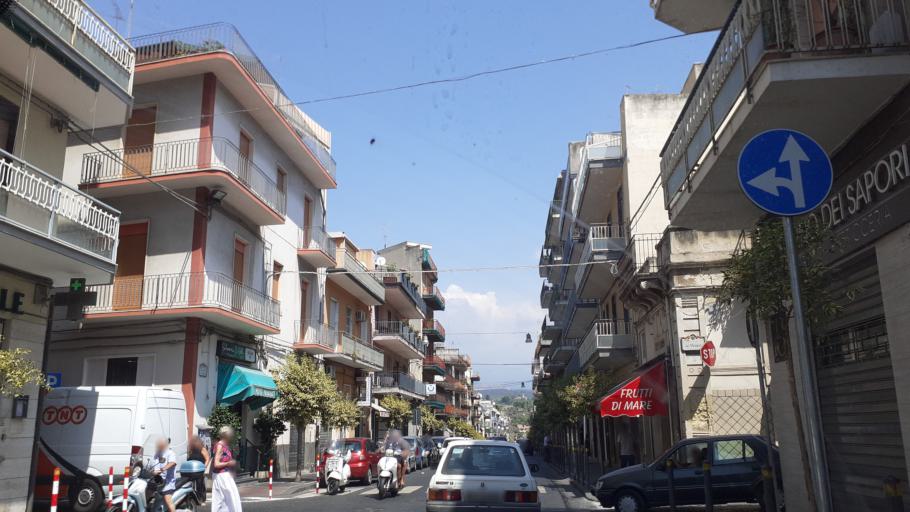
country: IT
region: Sicily
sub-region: Catania
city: Belvedere-Piano Tavola
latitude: 37.5190
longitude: 15.0071
